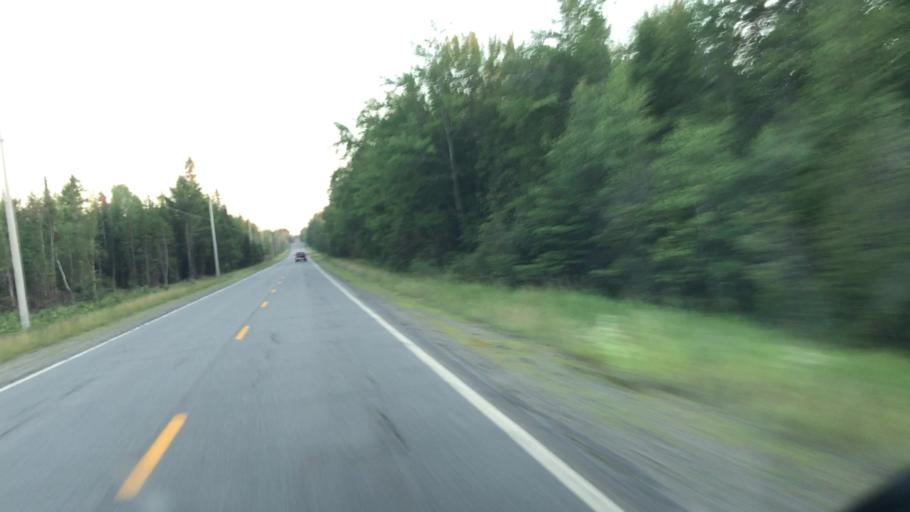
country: US
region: Maine
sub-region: Penobscot County
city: Medway
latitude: 45.6067
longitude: -68.3071
